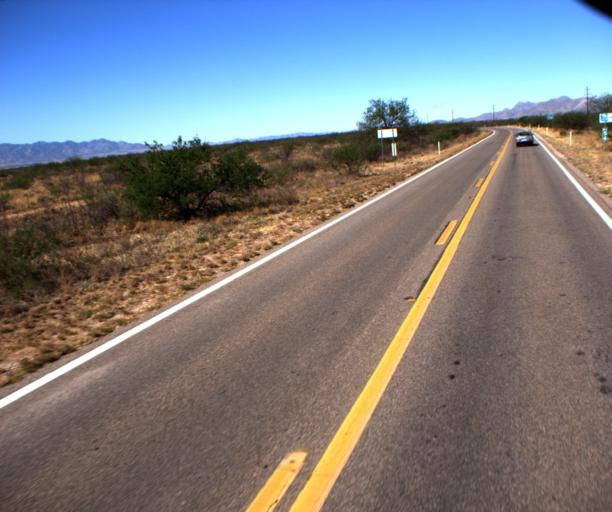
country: US
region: Arizona
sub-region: Cochise County
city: Huachuca City
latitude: 31.7087
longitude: -110.2791
